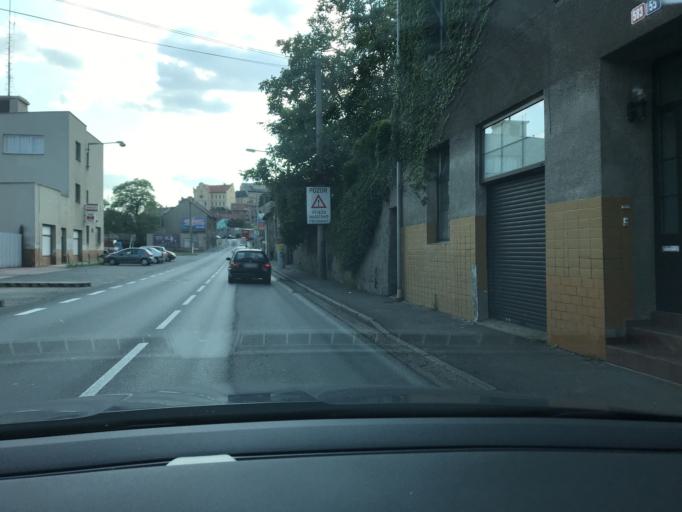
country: CZ
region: Central Bohemia
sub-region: Okres Kladno
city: Slany
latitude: 50.2336
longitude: 14.0921
